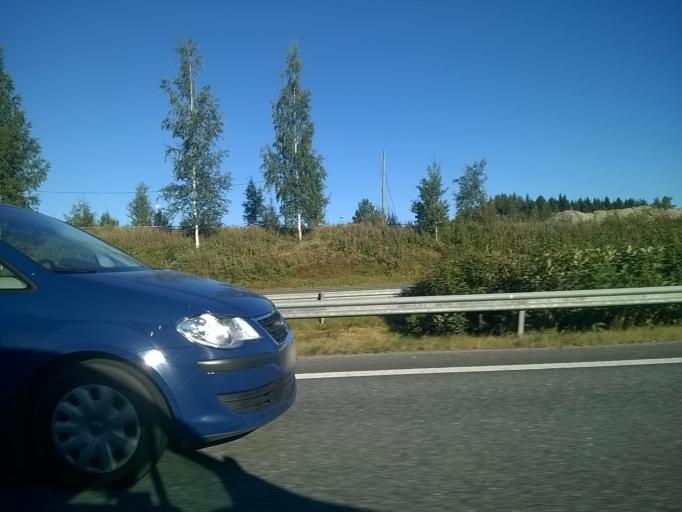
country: FI
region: Pirkanmaa
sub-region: Tampere
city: Tampere
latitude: 61.4801
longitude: 23.8720
